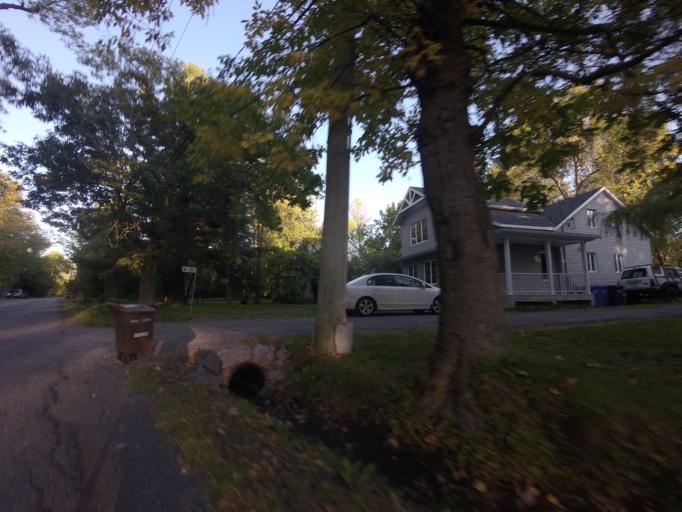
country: CA
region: Quebec
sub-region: Monteregie
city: Hudson
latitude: 45.4817
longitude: -74.2199
